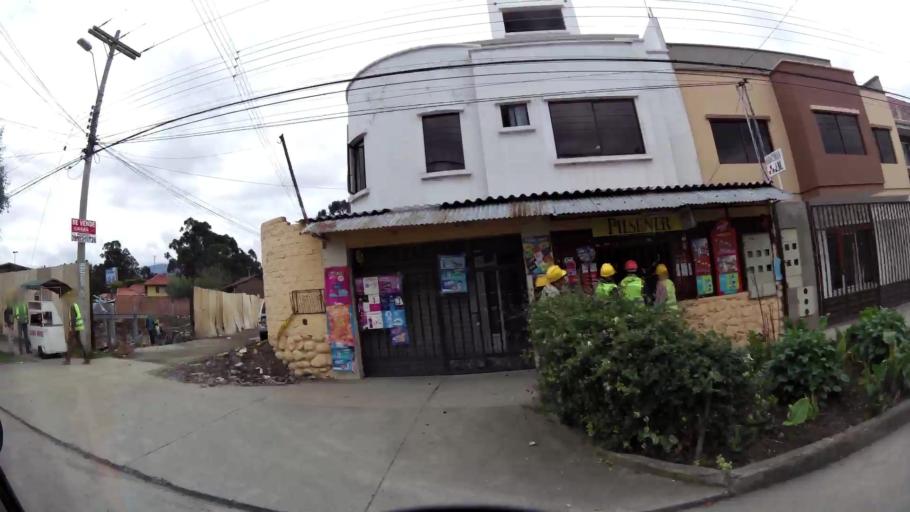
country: EC
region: Azuay
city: Cuenca
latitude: -2.9106
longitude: -79.0187
